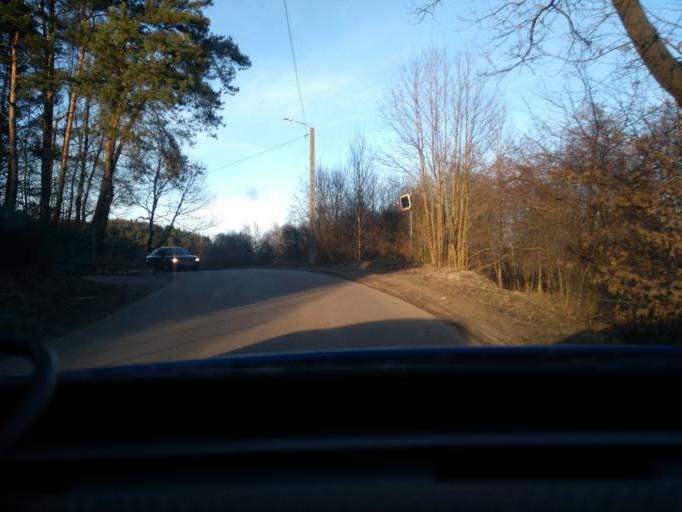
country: PL
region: Pomeranian Voivodeship
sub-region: Powiat kartuski
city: Przodkowo
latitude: 54.3793
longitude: 18.2659
